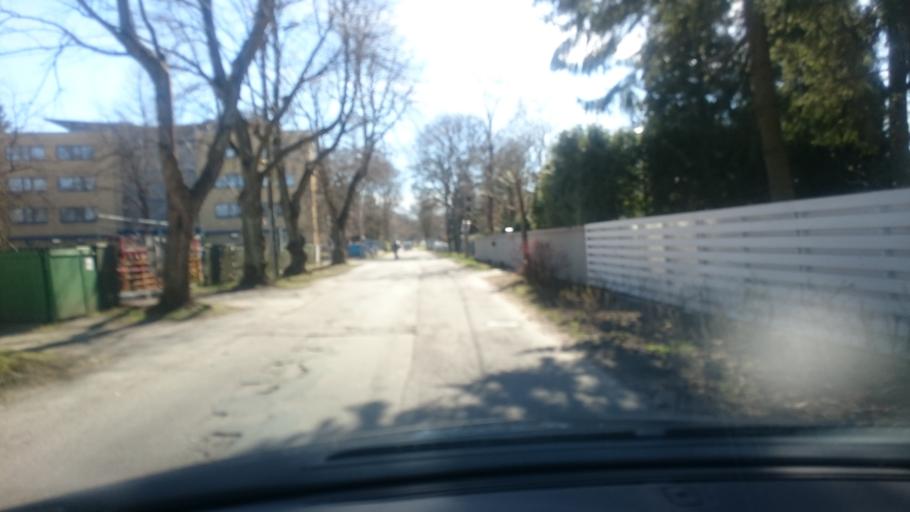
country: EE
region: Harju
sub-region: Viimsi vald
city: Viimsi
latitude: 59.4641
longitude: 24.8256
